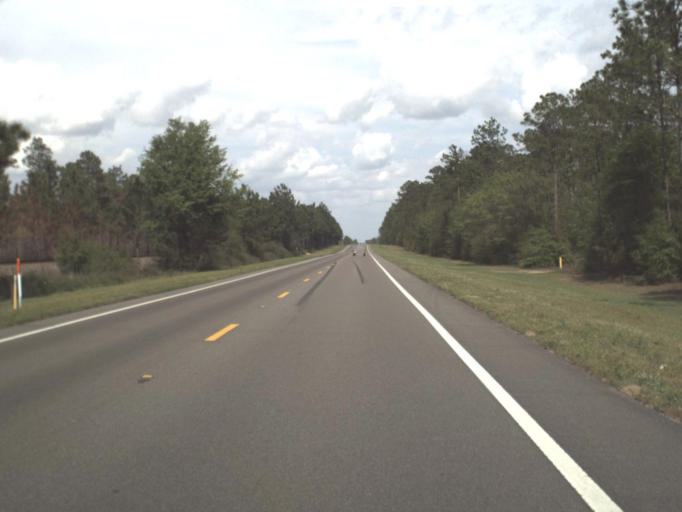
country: US
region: Florida
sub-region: Santa Rosa County
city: East Milton
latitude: 30.6893
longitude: -86.8179
